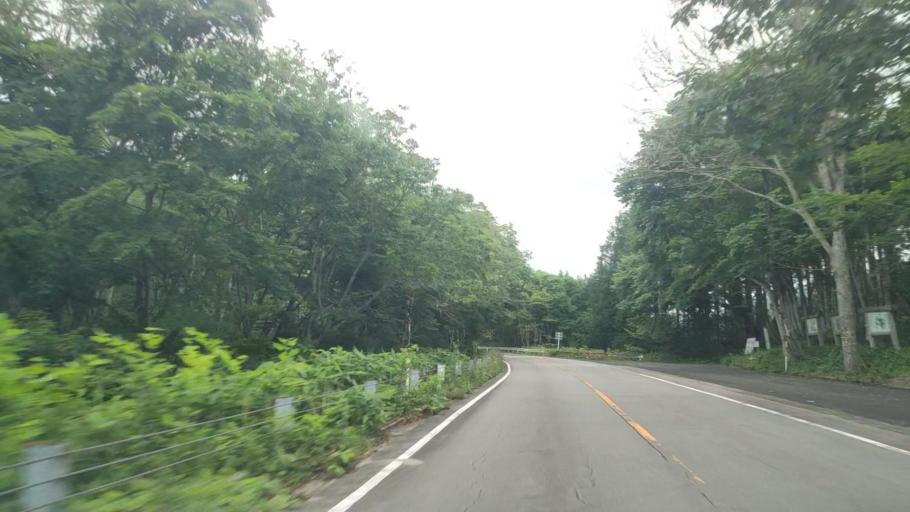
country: JP
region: Tottori
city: Kurayoshi
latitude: 35.3146
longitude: 133.6107
